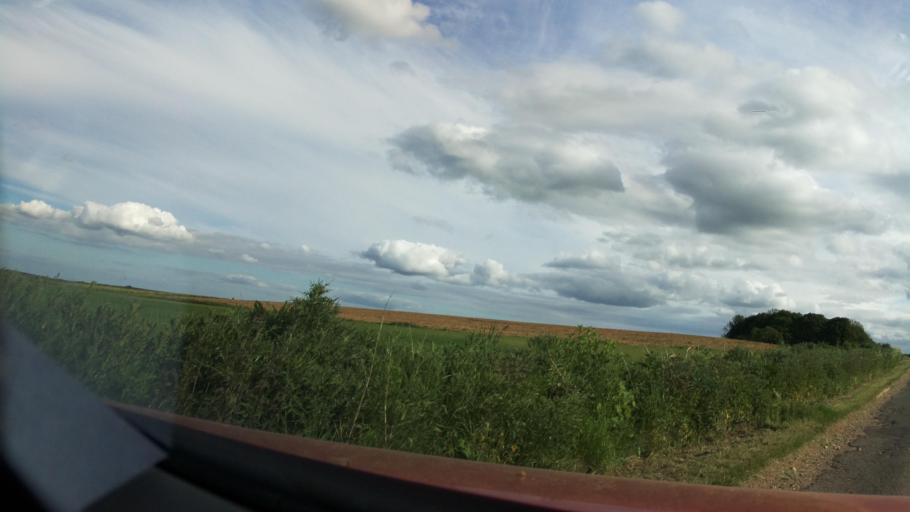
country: GB
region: England
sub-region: Gloucestershire
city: Westfield
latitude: 51.8917
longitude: -1.8873
